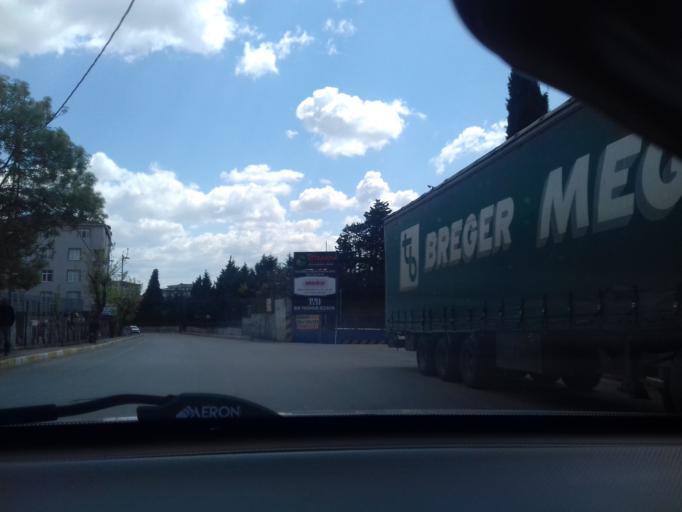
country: TR
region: Istanbul
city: Pendik
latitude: 40.8883
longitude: 29.2806
